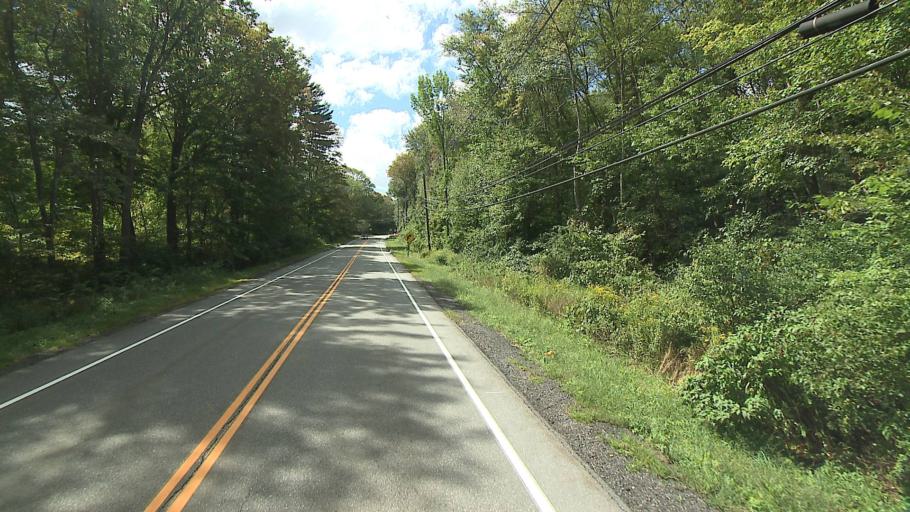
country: US
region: Connecticut
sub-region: Tolland County
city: Storrs
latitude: 41.8315
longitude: -72.2563
